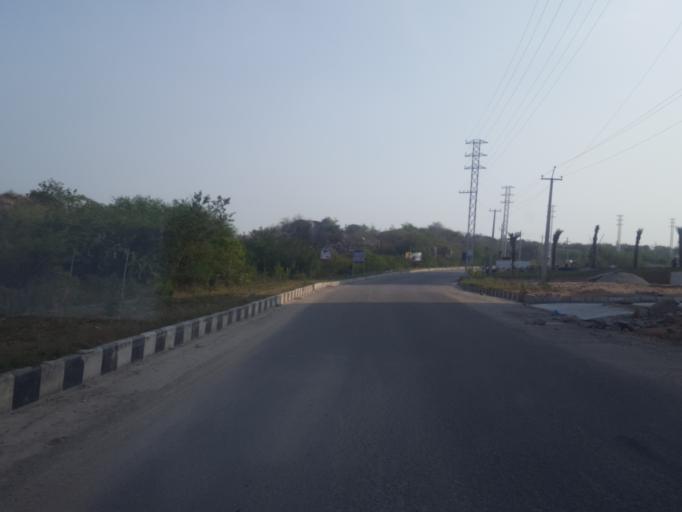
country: IN
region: Telangana
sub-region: Medak
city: Serilingampalle
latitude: 17.4079
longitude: 78.3153
